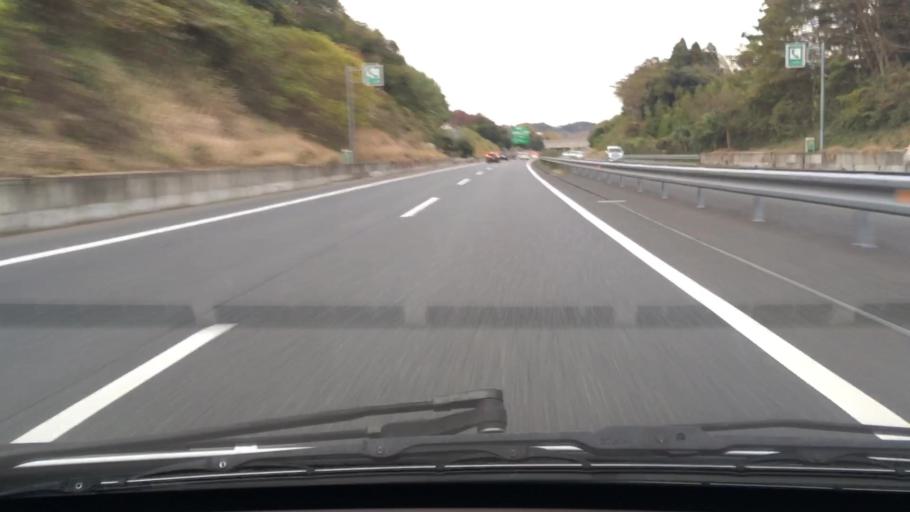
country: JP
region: Chiba
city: Kisarazu
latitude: 35.3360
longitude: 139.9448
